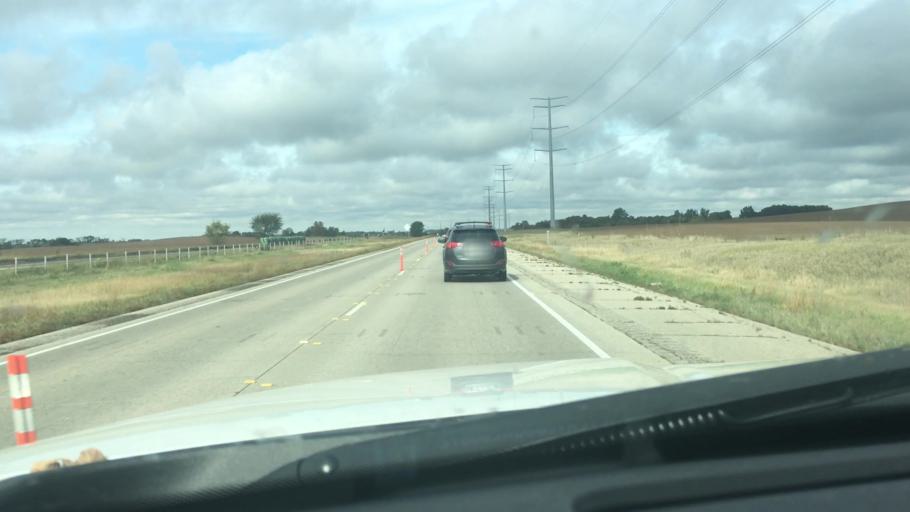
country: US
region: Minnesota
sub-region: Douglas County
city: Alexandria
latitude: 45.9234
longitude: -95.5638
